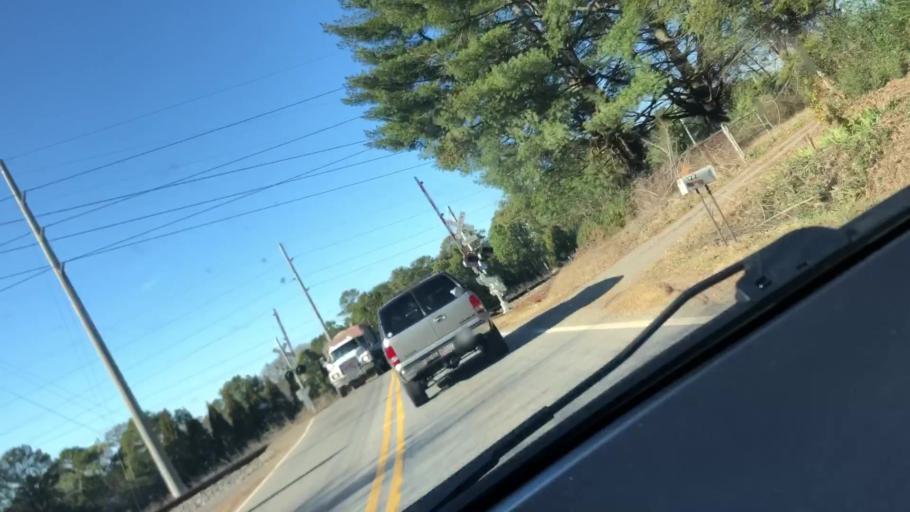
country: US
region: Georgia
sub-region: Bartow County
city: Cartersville
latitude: 34.2125
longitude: -84.8014
